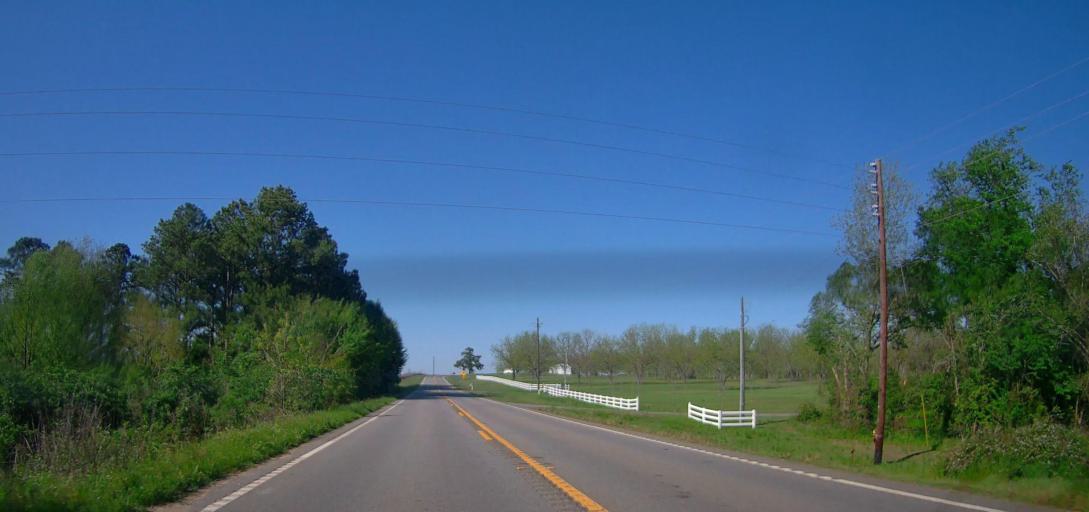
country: US
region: Georgia
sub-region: Pulaski County
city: Hawkinsville
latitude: 32.1705
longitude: -83.5111
